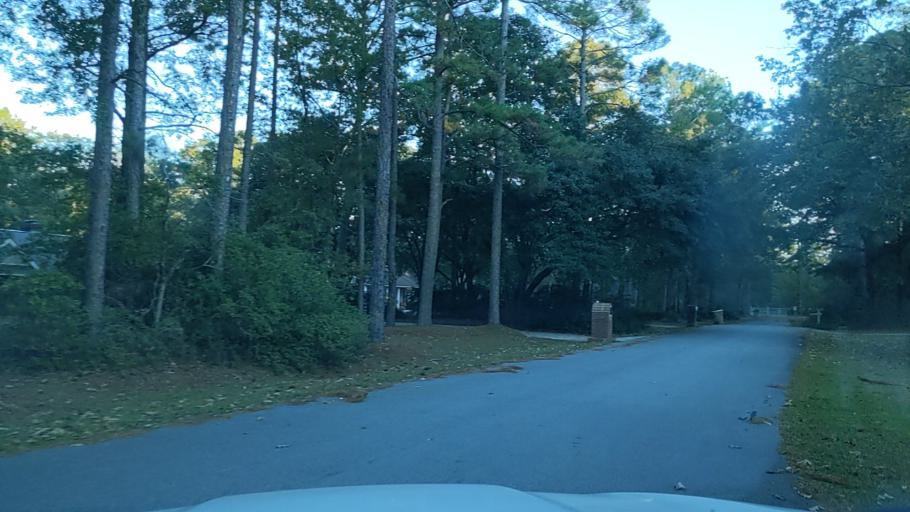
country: US
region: Georgia
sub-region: Effingham County
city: Rincon
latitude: 32.2670
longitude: -81.2071
